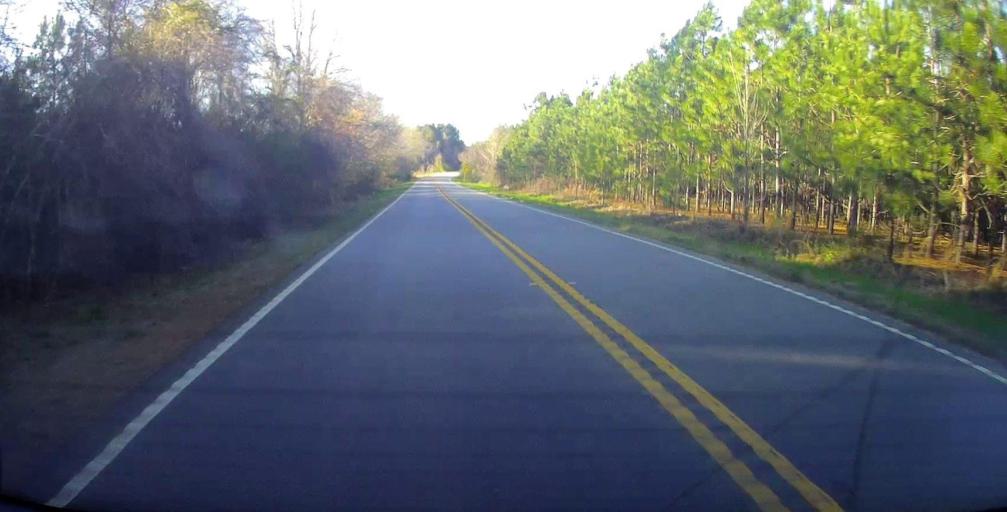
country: US
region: Georgia
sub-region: Wilcox County
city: Abbeville
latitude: 32.1341
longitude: -83.3377
